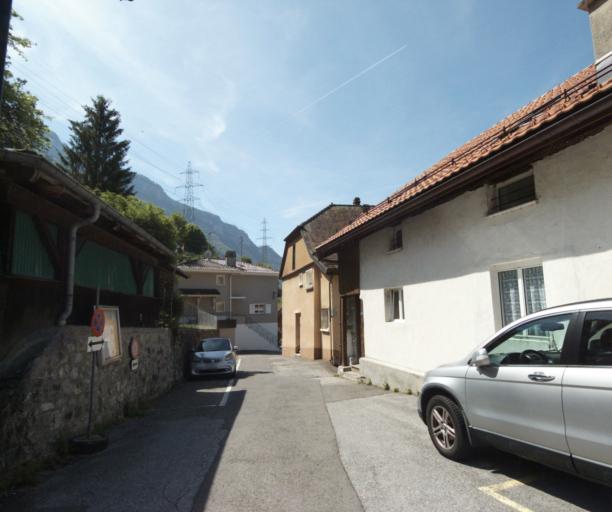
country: CH
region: Vaud
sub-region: Aigle District
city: Villeneuve
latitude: 46.4002
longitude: 6.9398
